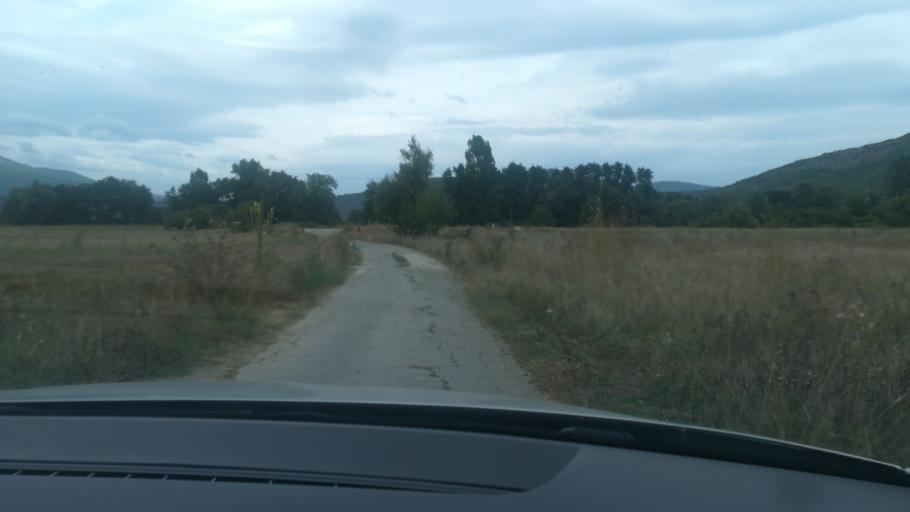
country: MK
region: Debarca
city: Belcista
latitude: 41.2965
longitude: 20.8312
